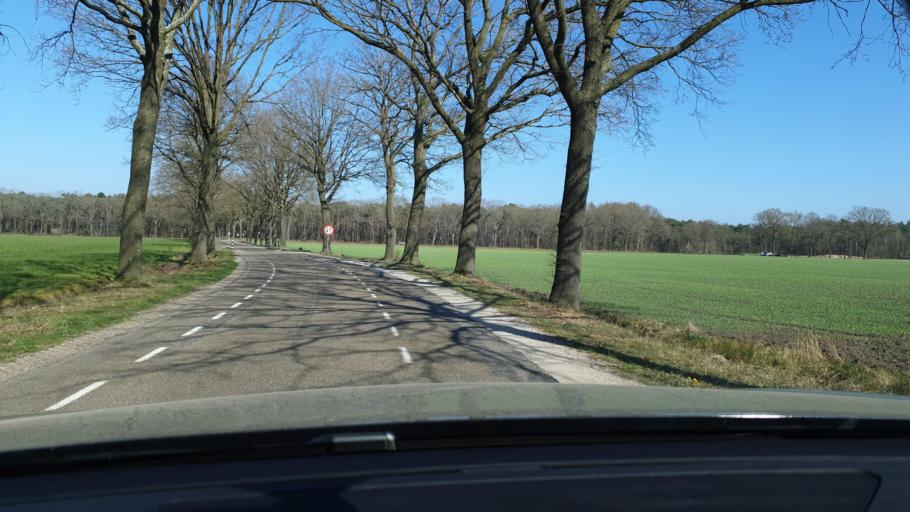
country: NL
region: North Brabant
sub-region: Bergeijk
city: Bergeyk
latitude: 51.3658
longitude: 5.3857
